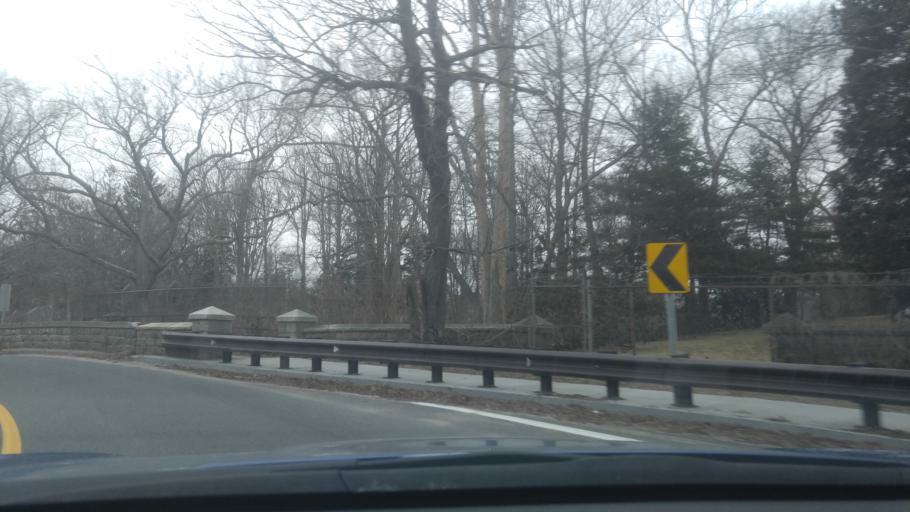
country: US
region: Rhode Island
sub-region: Washington County
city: Wakefield-Peacedale
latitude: 41.4511
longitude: -71.4956
